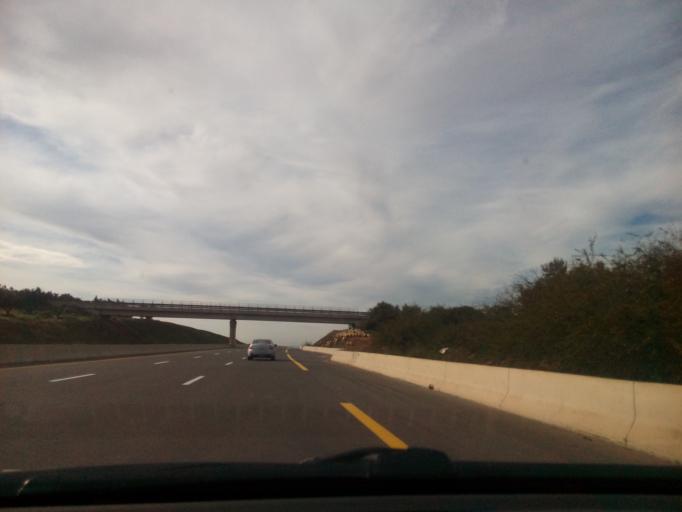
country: DZ
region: Sidi Bel Abbes
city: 'Ain el Berd
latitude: 35.3371
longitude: -0.5200
